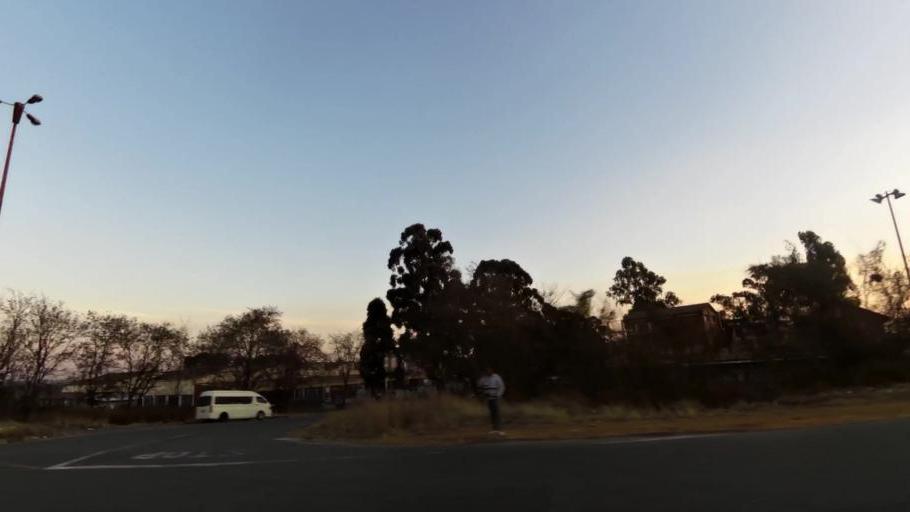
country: ZA
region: Gauteng
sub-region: City of Johannesburg Metropolitan Municipality
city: Johannesburg
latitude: -26.2029
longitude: 27.9842
